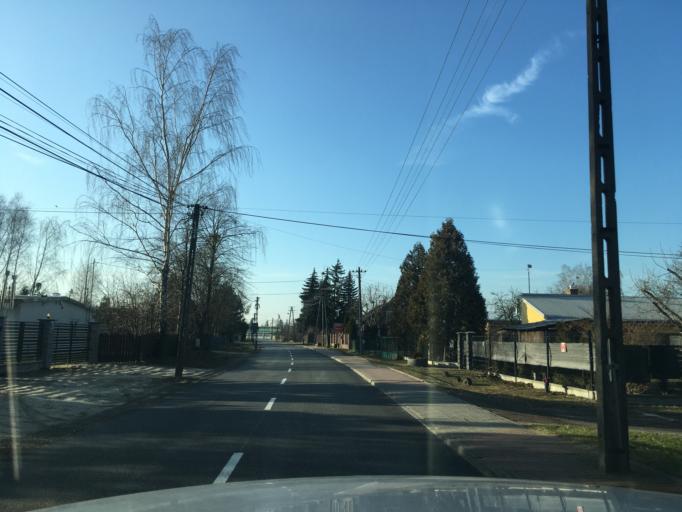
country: PL
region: Lodz Voivodeship
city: Zabia Wola
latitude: 52.0532
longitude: 20.7286
